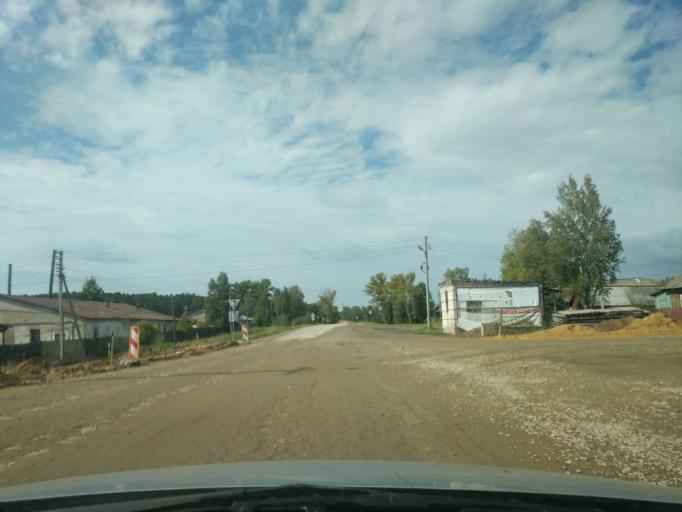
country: RU
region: Kostroma
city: Sudislavl'
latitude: 57.8771
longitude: 41.7285
